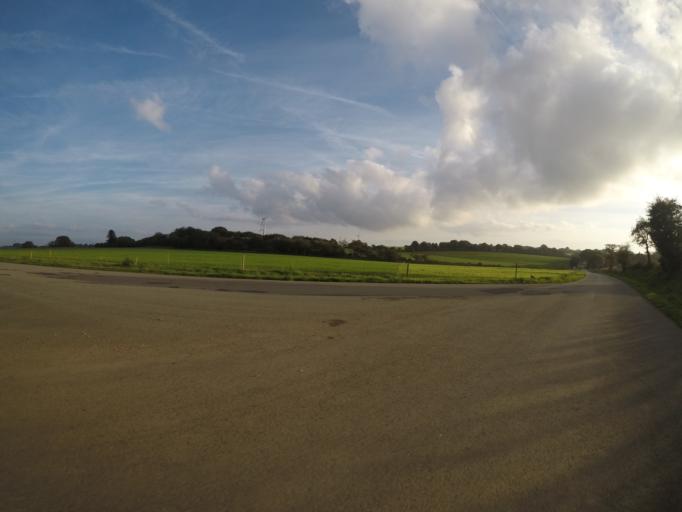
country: FR
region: Brittany
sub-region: Departement des Cotes-d'Armor
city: Louargat
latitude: 48.4776
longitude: -3.2901
